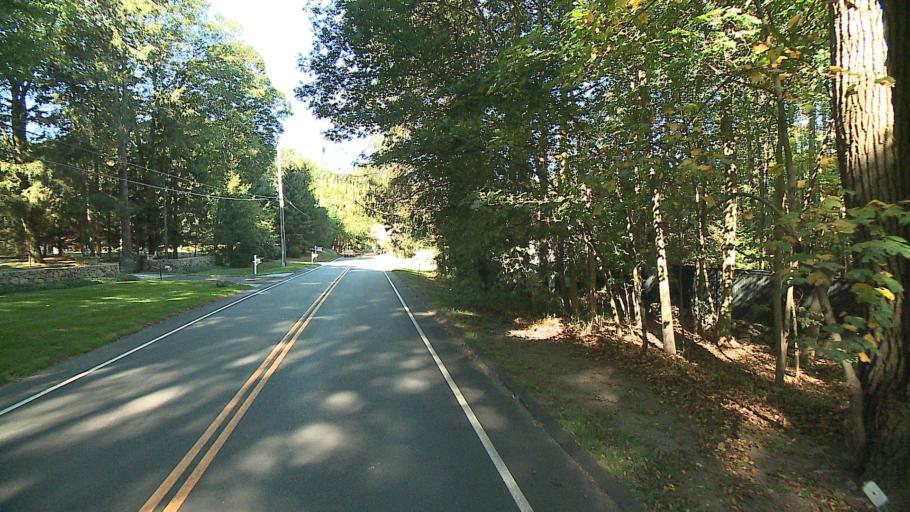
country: US
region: New York
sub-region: Westchester County
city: Pound Ridge
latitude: 41.1860
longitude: -73.5382
